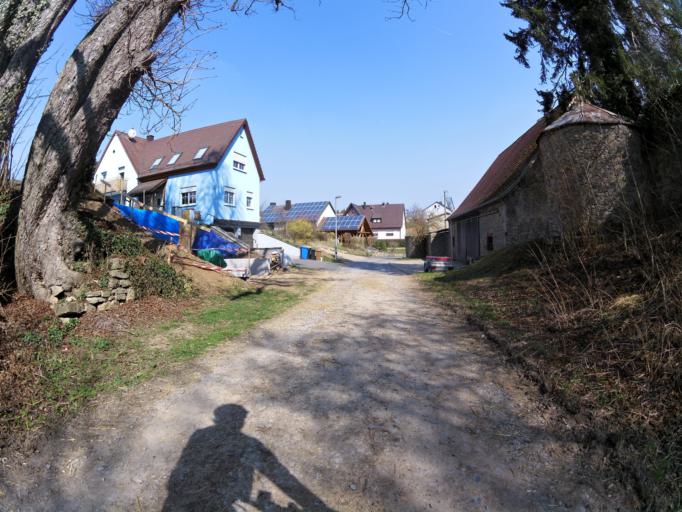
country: DE
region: Bavaria
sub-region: Regierungsbezirk Unterfranken
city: Winterhausen
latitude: 49.6749
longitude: 9.9929
